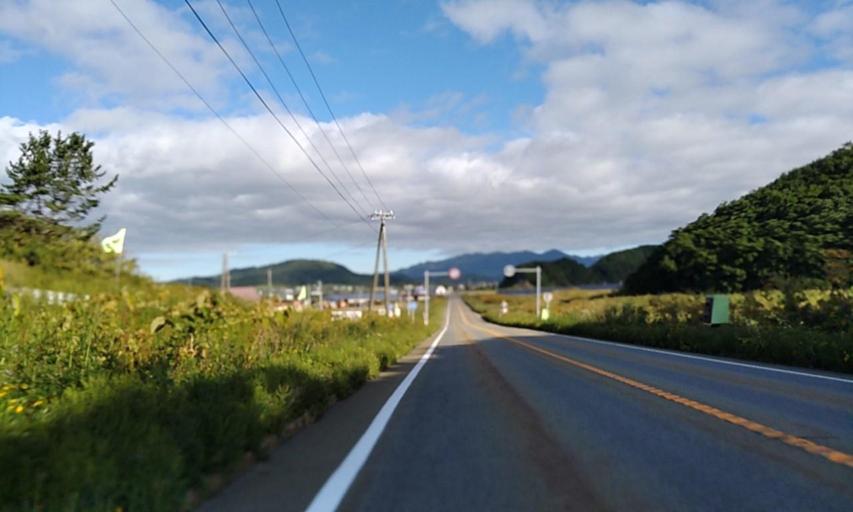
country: JP
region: Hokkaido
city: Shizunai-furukawacho
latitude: 42.2132
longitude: 142.6434
